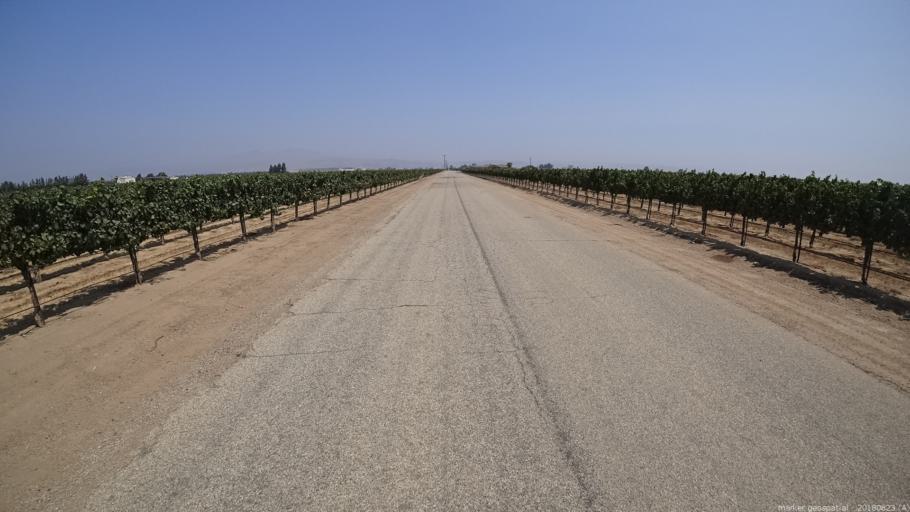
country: US
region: California
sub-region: Monterey County
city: Greenfield
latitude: 36.3212
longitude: -121.2744
